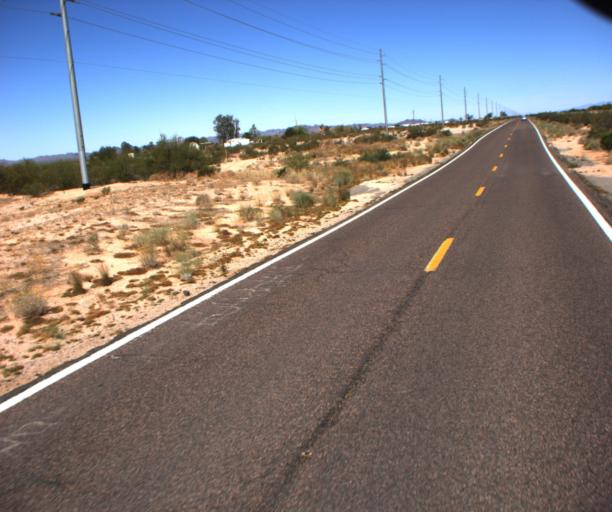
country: US
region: Arizona
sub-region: La Paz County
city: Salome
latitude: 33.8571
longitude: -113.9128
